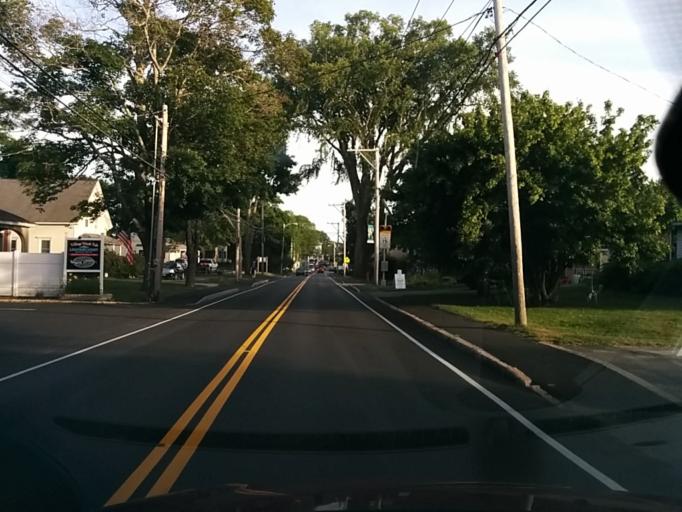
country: US
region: Maine
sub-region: Hancock County
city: Tremont
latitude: 44.2824
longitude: -68.3269
